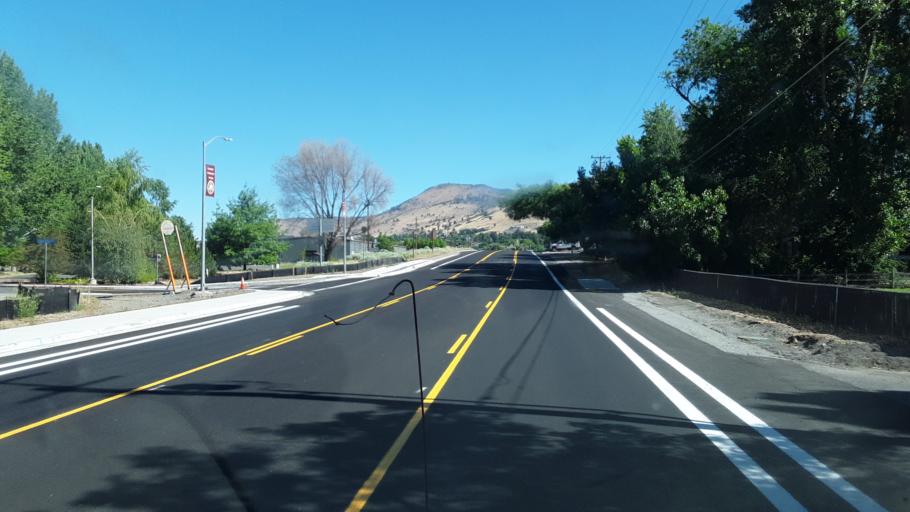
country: US
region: Oregon
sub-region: Klamath County
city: Altamont
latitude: 42.1922
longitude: -121.6980
